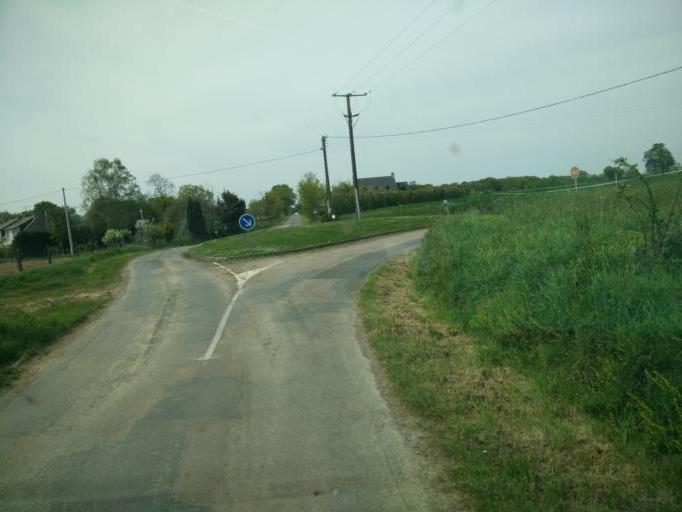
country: FR
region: Brittany
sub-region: Departement des Cotes-d'Armor
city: Matignon
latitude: 48.5868
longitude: -2.2531
